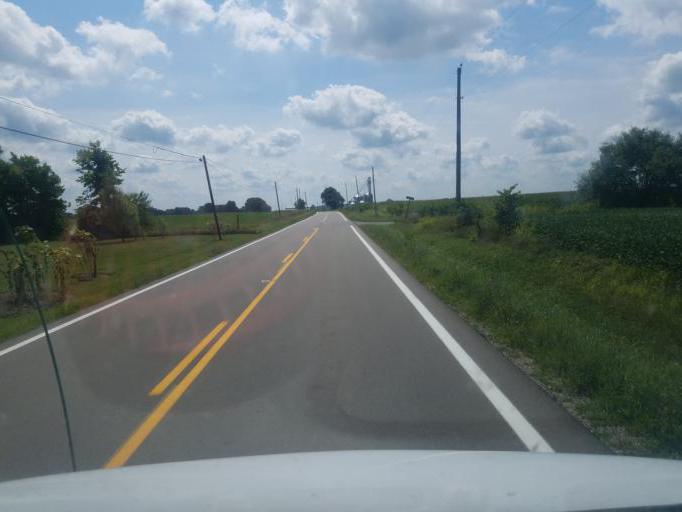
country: US
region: Ohio
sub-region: Marion County
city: Prospect
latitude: 40.3987
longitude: -83.1624
